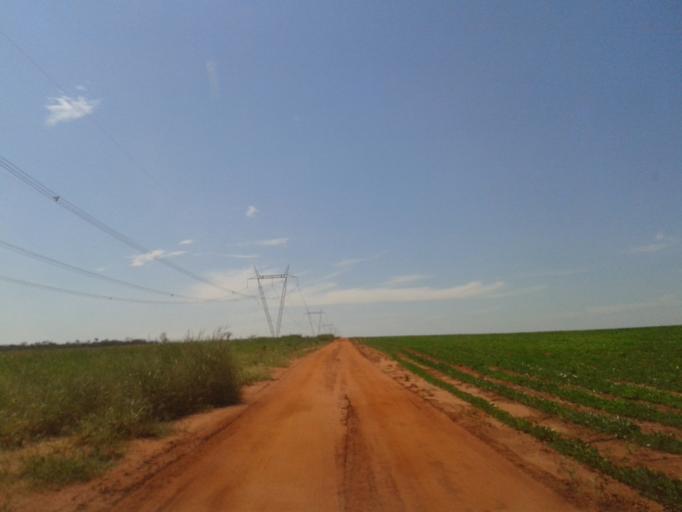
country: BR
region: Minas Gerais
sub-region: Santa Vitoria
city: Santa Vitoria
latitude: -19.0682
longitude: -50.4644
